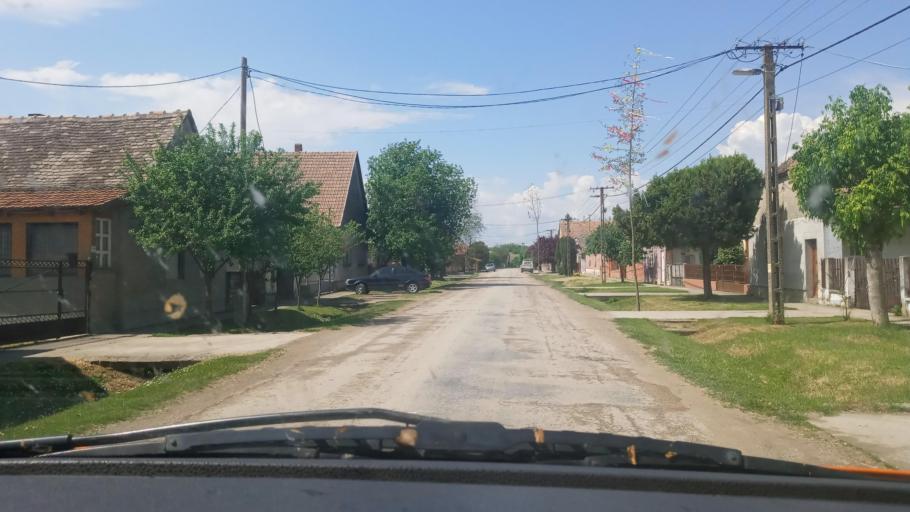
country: HU
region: Baranya
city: Beremend
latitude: 45.7883
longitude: 18.3527
